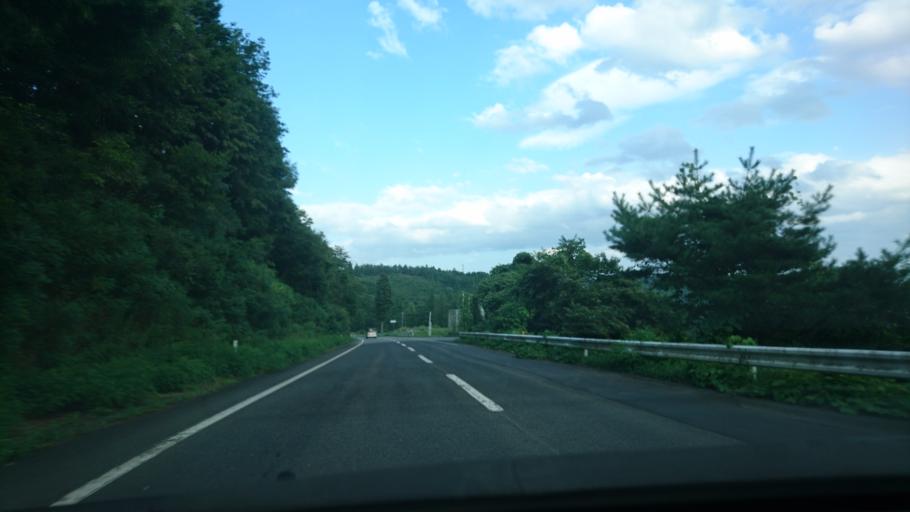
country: JP
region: Iwate
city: Mizusawa
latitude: 39.0306
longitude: 141.2807
